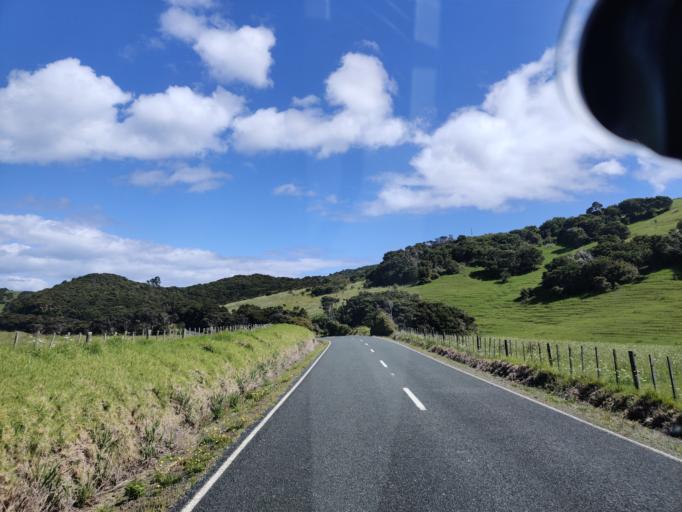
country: NZ
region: Northland
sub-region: Far North District
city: Paihia
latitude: -35.2703
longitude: 174.2781
